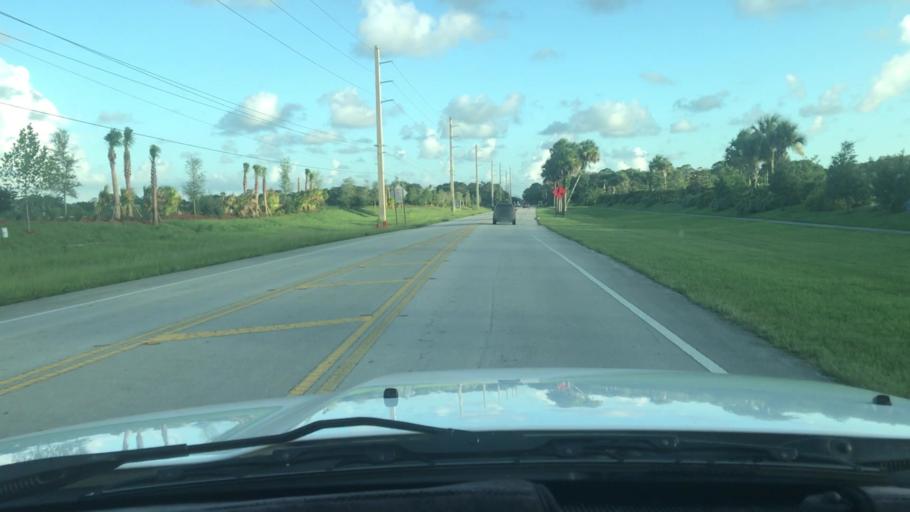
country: US
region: Florida
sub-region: Saint Lucie County
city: Lakewood Park
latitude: 27.5637
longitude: -80.4145
